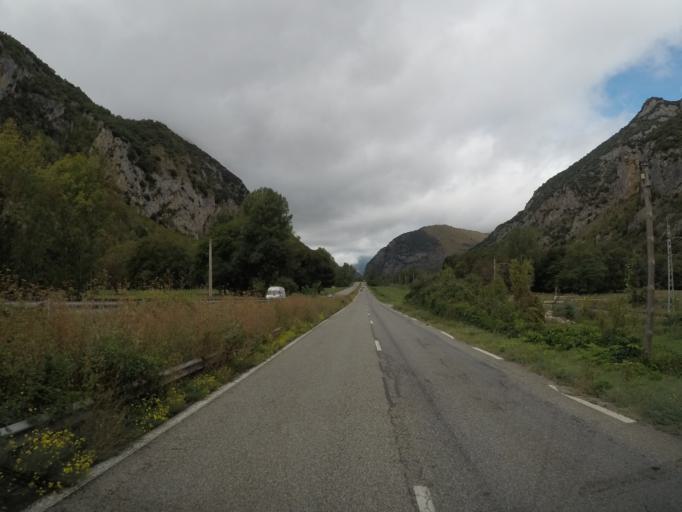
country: FR
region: Midi-Pyrenees
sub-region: Departement de l'Ariege
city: Tarascon-sur-Ariege
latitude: 42.8045
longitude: 1.6469
